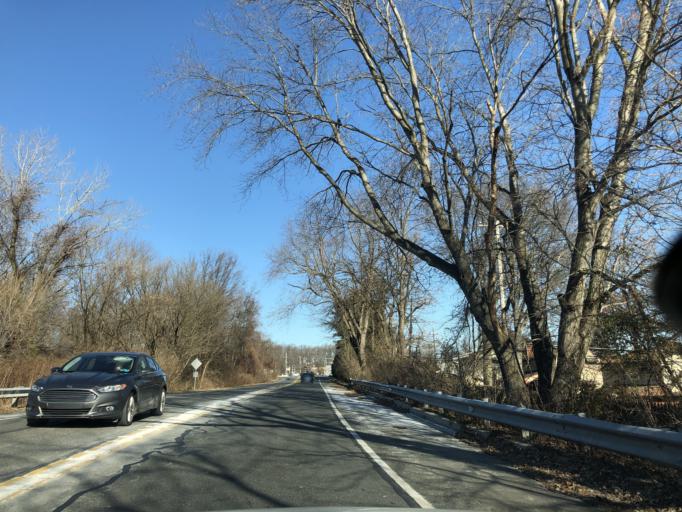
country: US
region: Pennsylvania
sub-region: Bucks County
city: Langhorne Manor
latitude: 40.1648
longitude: -74.8981
